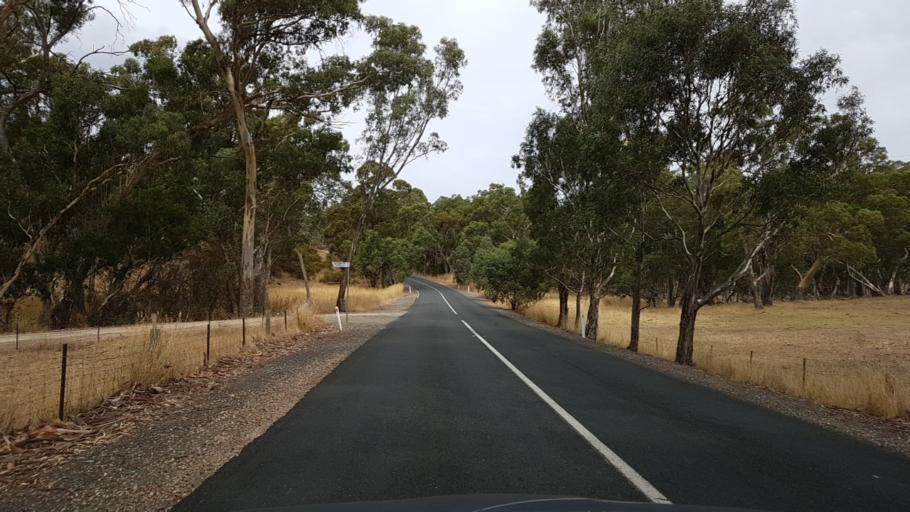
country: AU
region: South Australia
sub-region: Adelaide Hills
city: Birdwood
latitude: -34.7891
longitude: 138.9454
